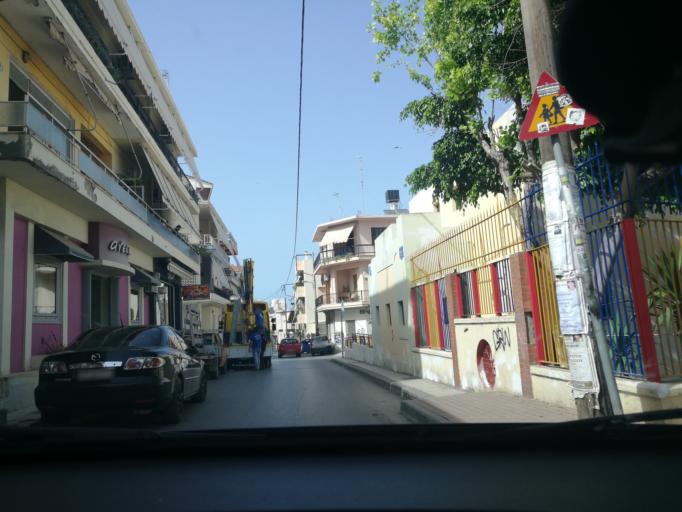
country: GR
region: Crete
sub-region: Nomos Irakleiou
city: Irakleion
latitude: 35.3252
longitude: 25.1300
